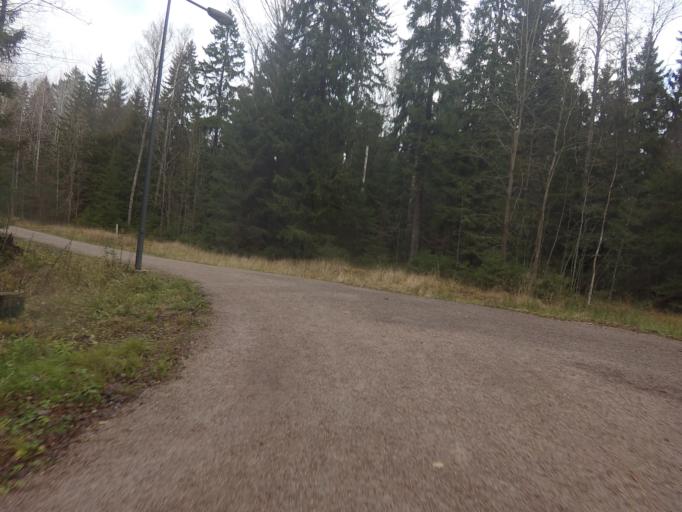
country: FI
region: Uusimaa
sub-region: Helsinki
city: Kauniainen
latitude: 60.1816
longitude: 24.7080
